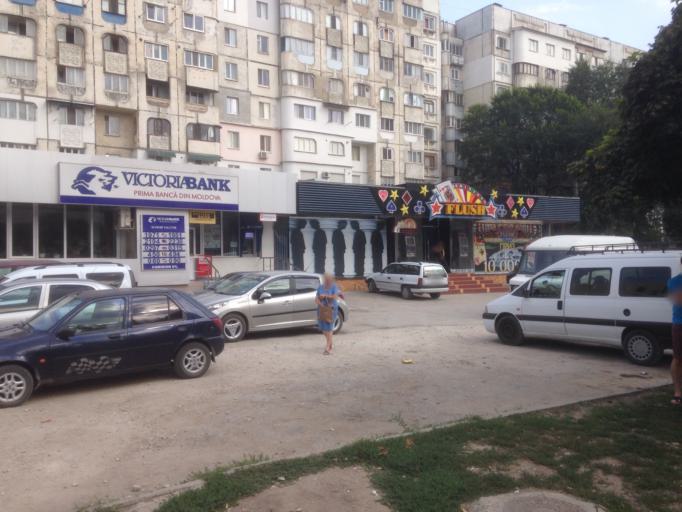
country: MD
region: Balti
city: Balti
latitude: 47.7665
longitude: 27.9364
